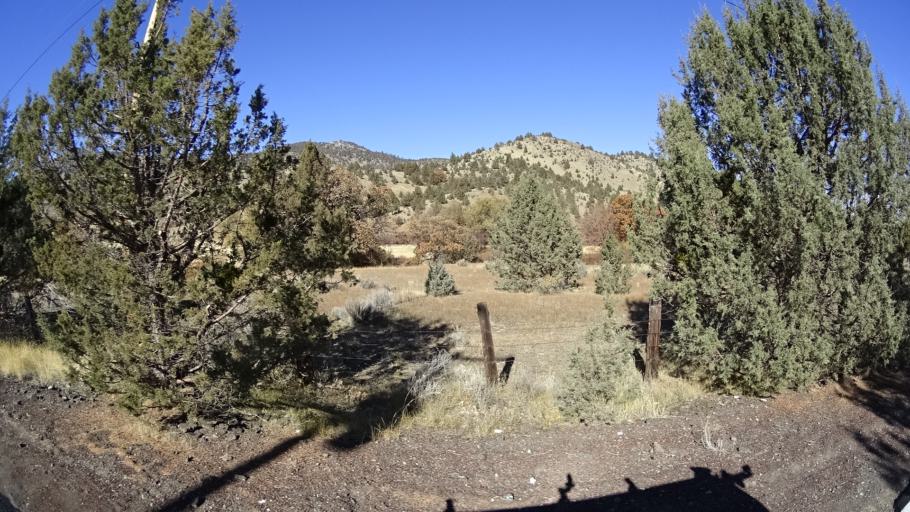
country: US
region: California
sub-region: Siskiyou County
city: Weed
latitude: 41.4725
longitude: -122.5826
